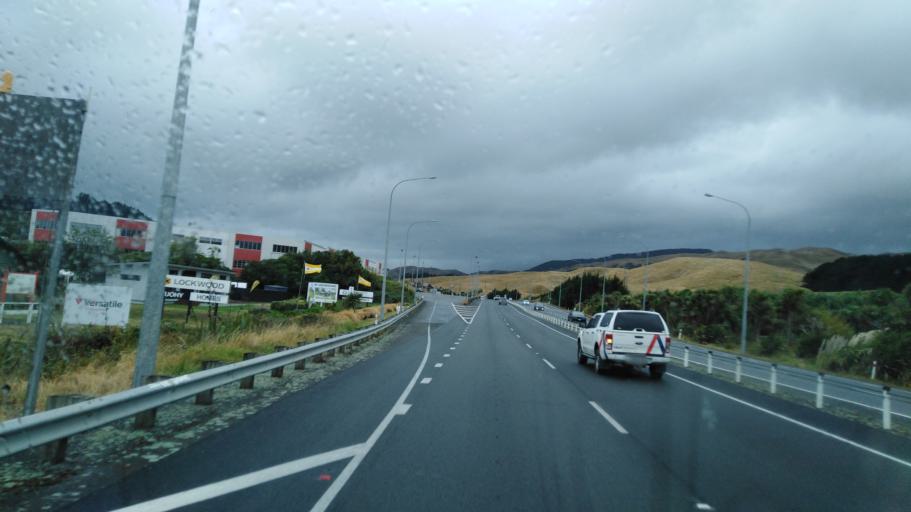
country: NZ
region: Wellington
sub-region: Porirua City
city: Porirua
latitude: -41.0796
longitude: 174.8717
